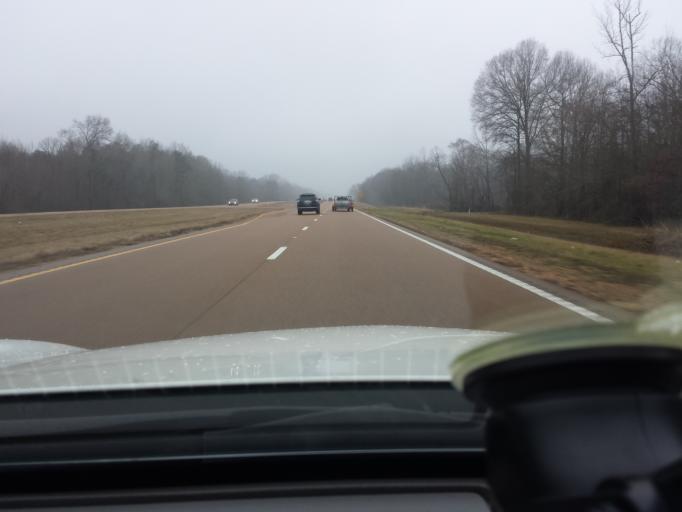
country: US
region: Mississippi
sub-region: Rankin County
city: Pelahatchie
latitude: 32.5343
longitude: -89.8233
